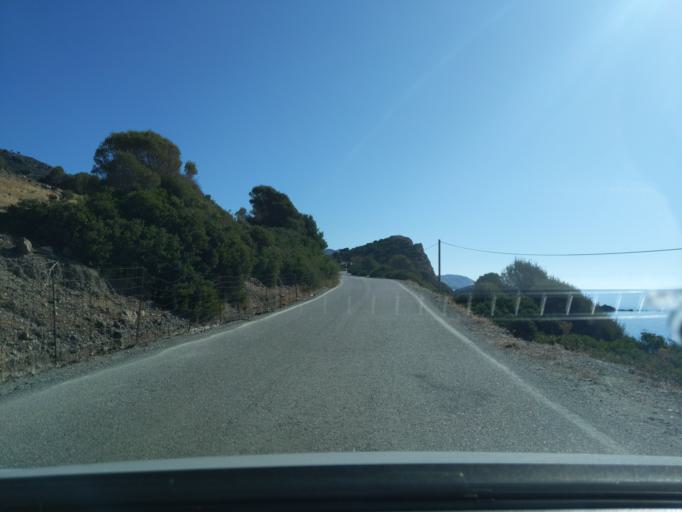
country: GR
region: Crete
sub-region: Nomos Irakleiou
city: Moires
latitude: 34.9377
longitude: 24.8105
